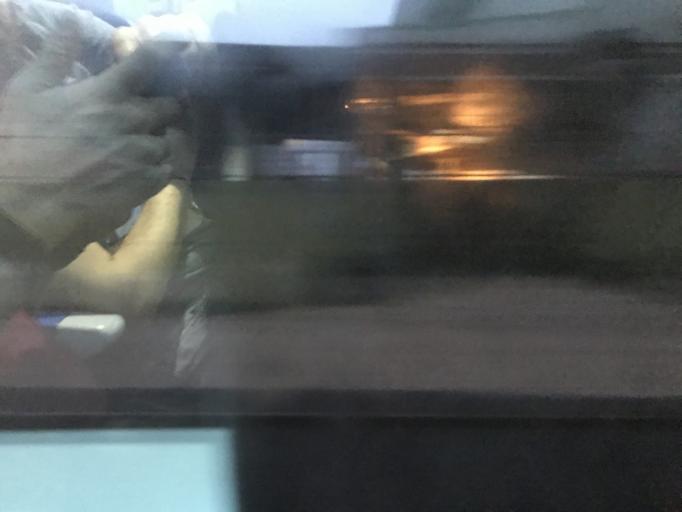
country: TR
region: Kocaeli
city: Korfez
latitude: 40.7720
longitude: 29.7252
